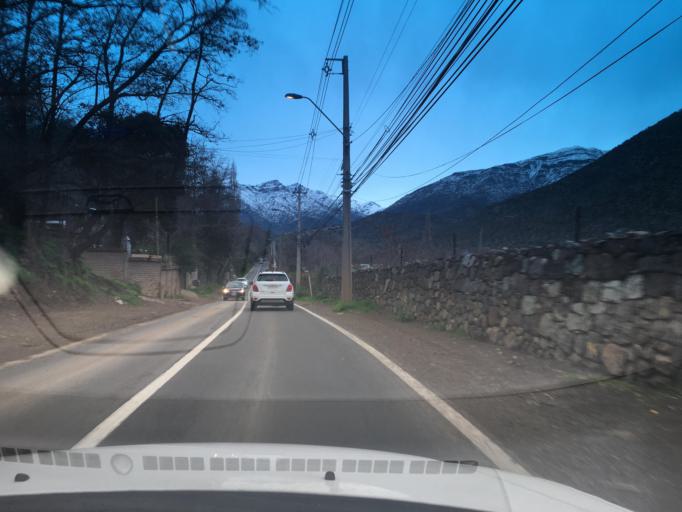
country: CL
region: Santiago Metropolitan
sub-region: Provincia de Cordillera
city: Puente Alto
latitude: -33.6611
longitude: -70.3504
